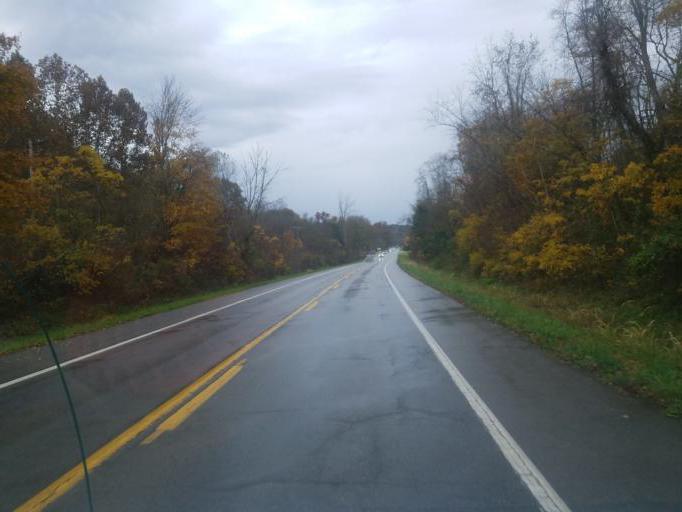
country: US
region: West Virginia
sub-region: Wood County
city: Boaz
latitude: 39.3623
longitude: -81.4941
